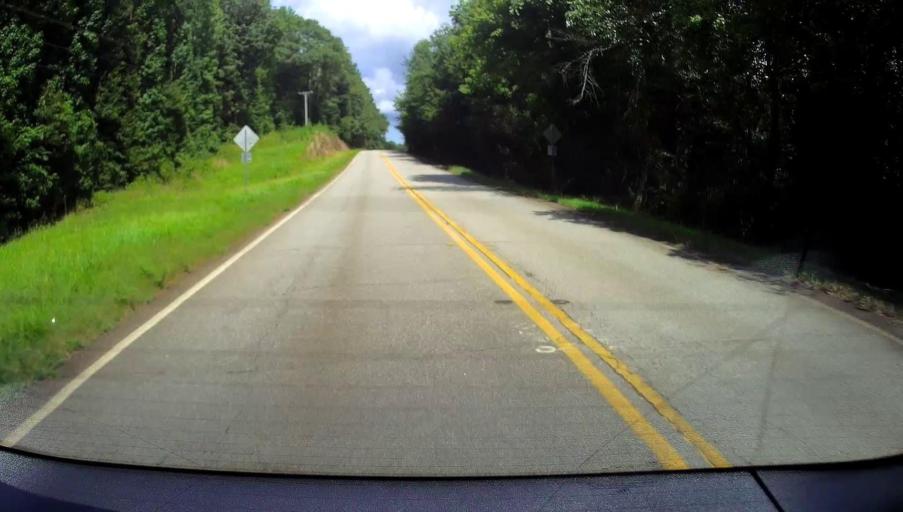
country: US
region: Georgia
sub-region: Crawford County
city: Knoxville
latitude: 32.8821
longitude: -84.0226
